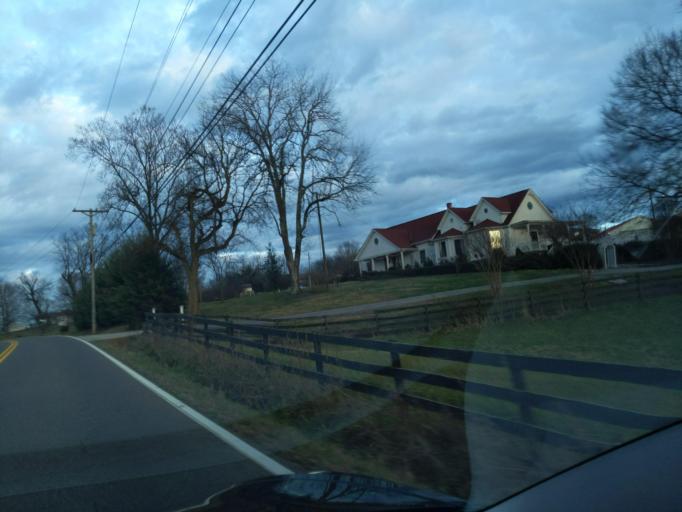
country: US
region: Tennessee
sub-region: Jefferson County
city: Dandridge
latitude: 35.9994
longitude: -83.4414
